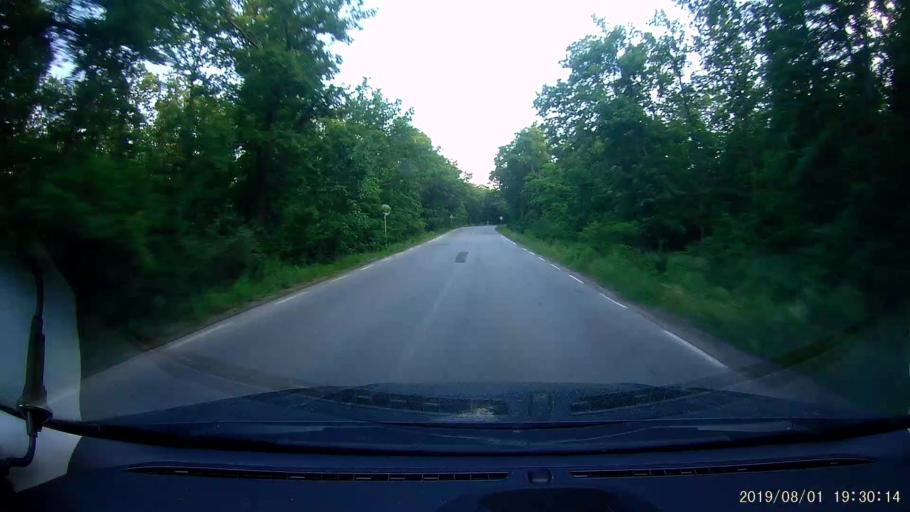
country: BG
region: Burgas
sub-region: Obshtina Sungurlare
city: Sungurlare
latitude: 42.8167
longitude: 26.8945
